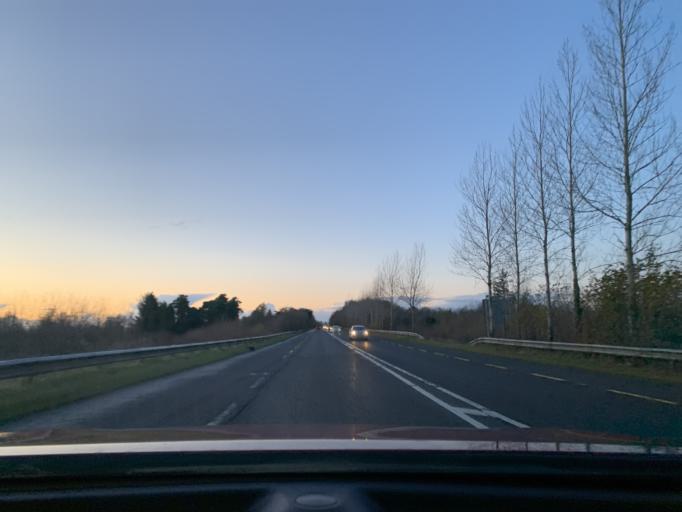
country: IE
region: Connaught
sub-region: County Leitrim
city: Carrick-on-Shannon
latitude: 53.9340
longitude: -8.0464
